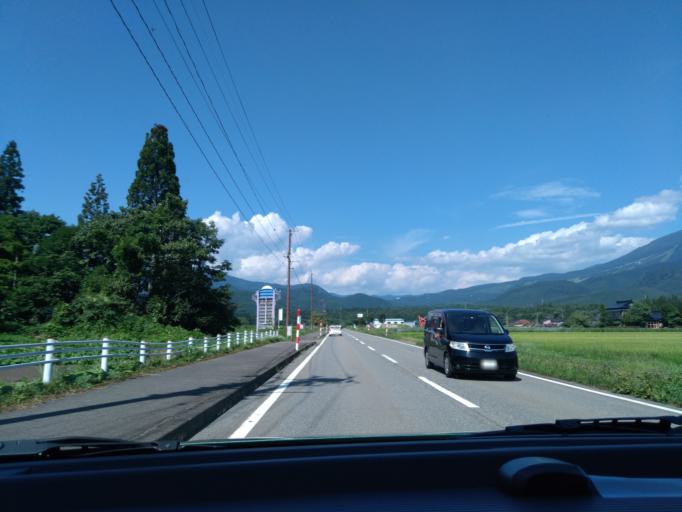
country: JP
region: Akita
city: Kakunodatemachi
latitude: 39.7379
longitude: 140.7097
